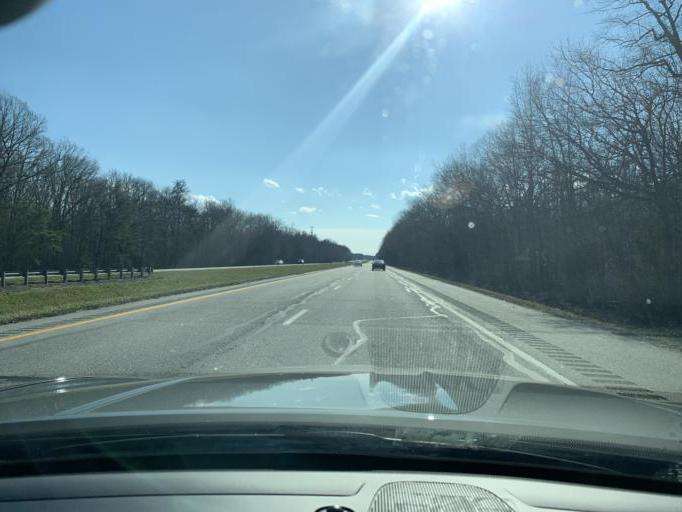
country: US
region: Delaware
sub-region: New Castle County
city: Townsend
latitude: 39.3046
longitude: -75.8507
